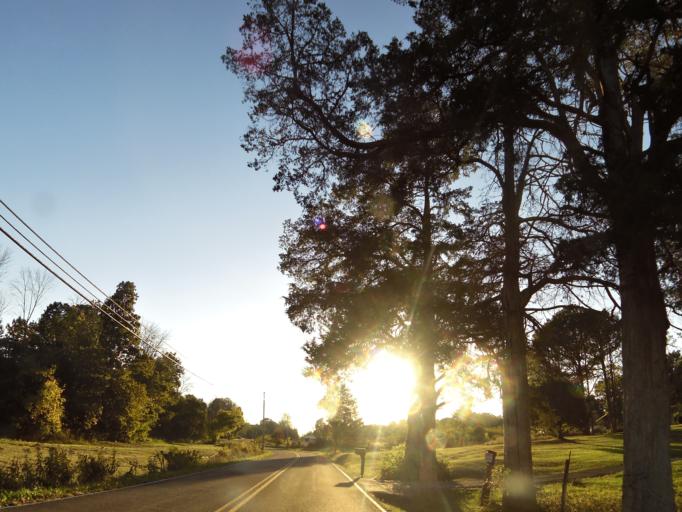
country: US
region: Tennessee
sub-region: Grainger County
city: Rutledge
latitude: 36.3094
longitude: -83.5555
